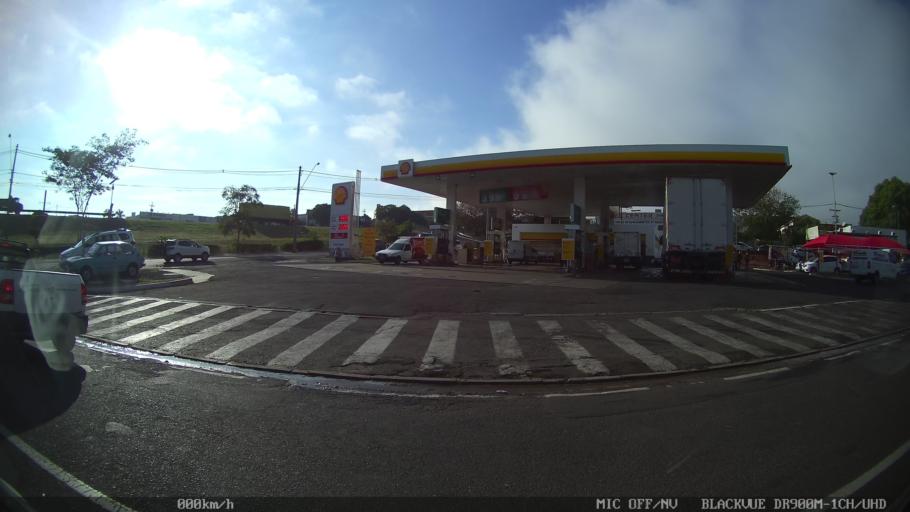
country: BR
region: Sao Paulo
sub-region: Sao Jose Do Rio Preto
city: Sao Jose do Rio Preto
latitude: -20.8272
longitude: -49.3660
